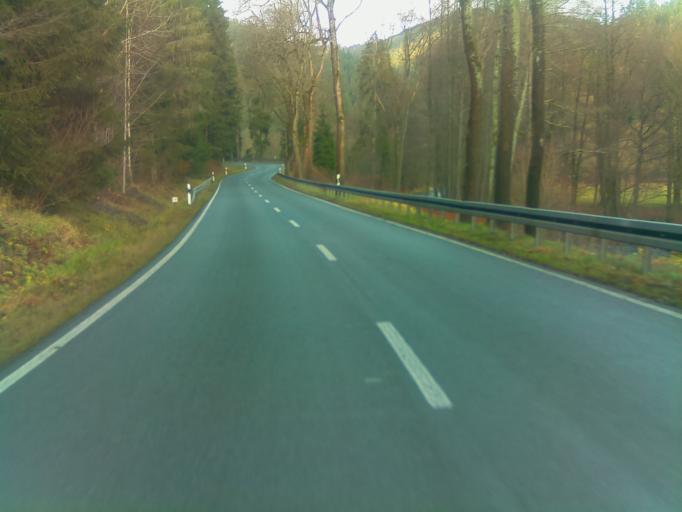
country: DE
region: Thuringia
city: Wildenspring
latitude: 50.5942
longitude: 11.0825
